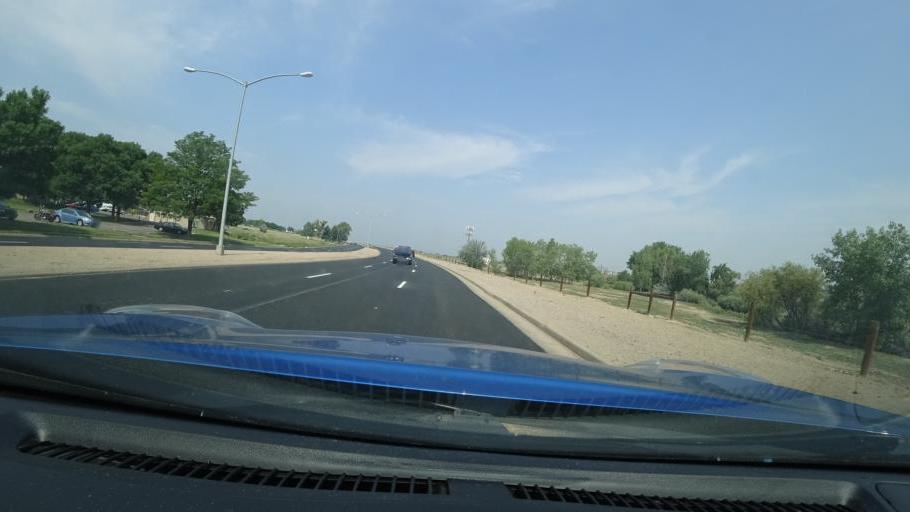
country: US
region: Colorado
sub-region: Adams County
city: Aurora
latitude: 39.7047
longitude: -104.7776
